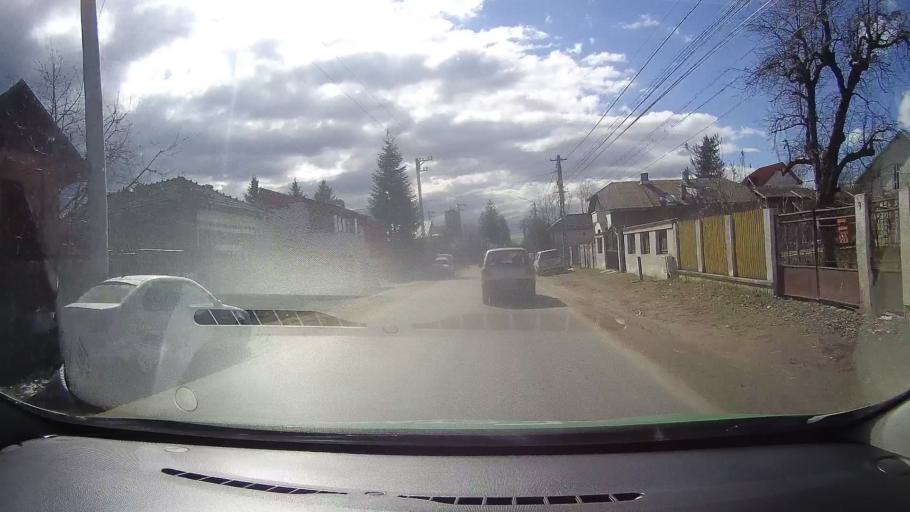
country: RO
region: Dambovita
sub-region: Comuna Branesti
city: Branesti
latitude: 45.0453
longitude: 25.4229
